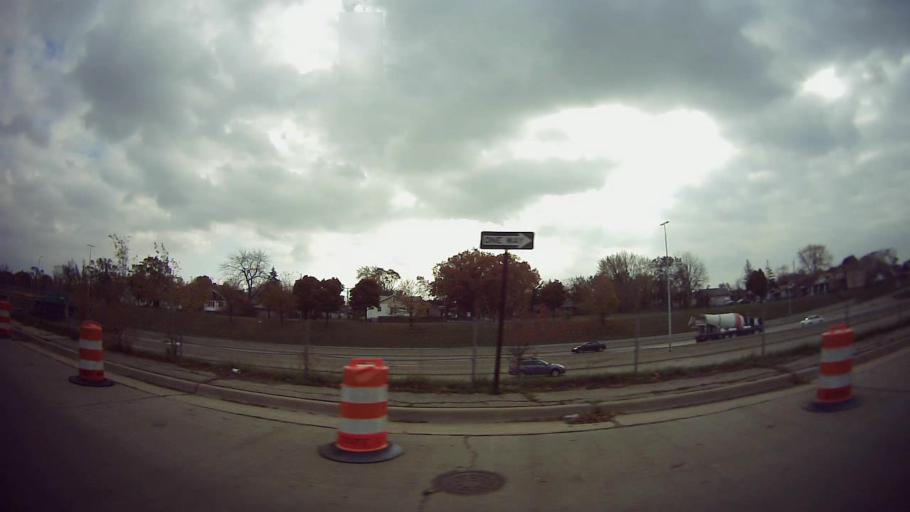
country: US
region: Michigan
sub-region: Wayne County
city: Highland Park
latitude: 42.4053
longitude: -83.1368
